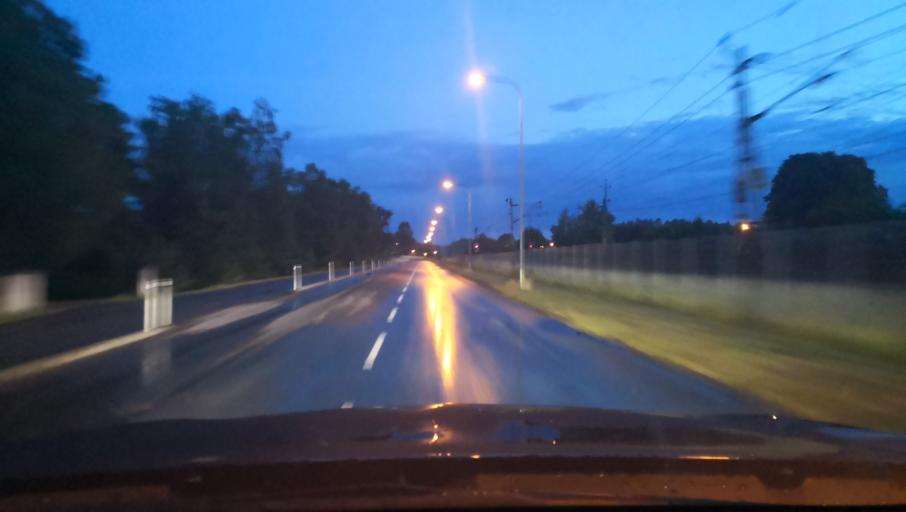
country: SE
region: Skane
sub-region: Osby Kommun
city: Osby
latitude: 56.3744
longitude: 13.9884
